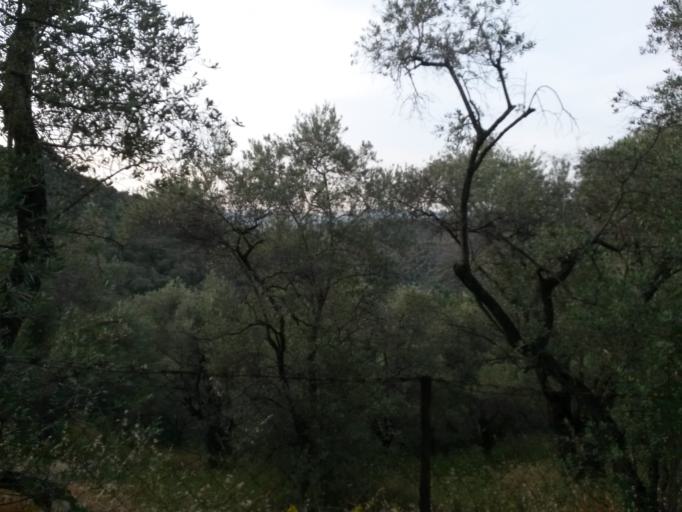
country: GR
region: North Aegean
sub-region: Nomos Lesvou
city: Agiasos
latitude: 39.0986
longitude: 26.3946
